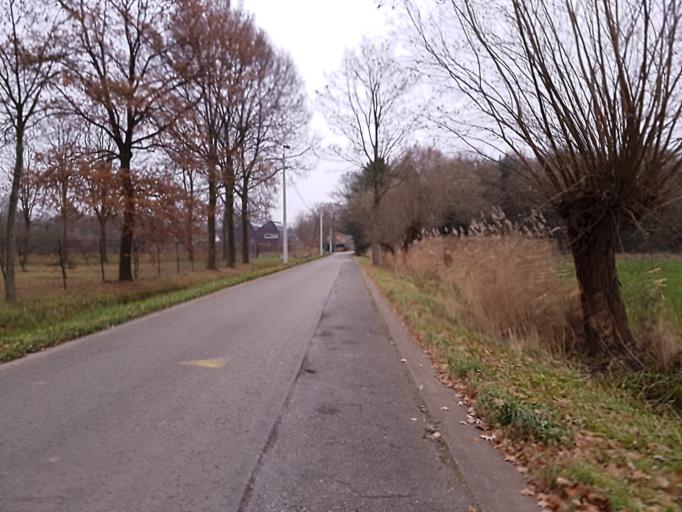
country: BE
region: Flanders
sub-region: Provincie Antwerpen
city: Rumst
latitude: 51.0703
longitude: 4.4035
